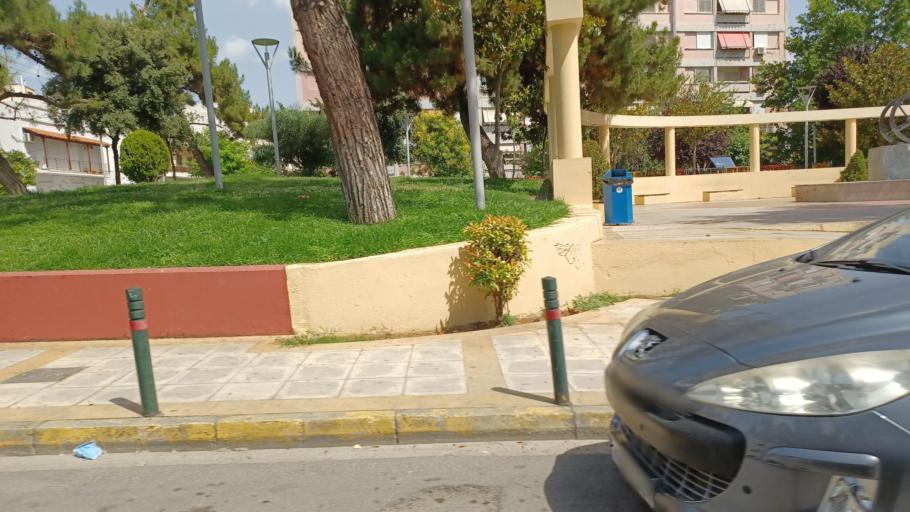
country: GR
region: Attica
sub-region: Nomarchia Athinas
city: Peristeri
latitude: 38.0155
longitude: 23.6936
